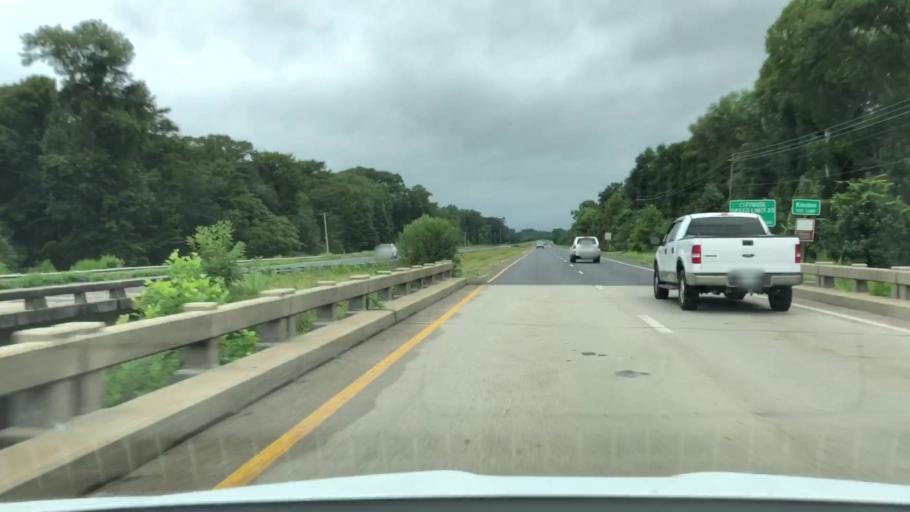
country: US
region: North Carolina
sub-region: Lenoir County
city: Kinston
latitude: 35.2614
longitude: -77.6194
